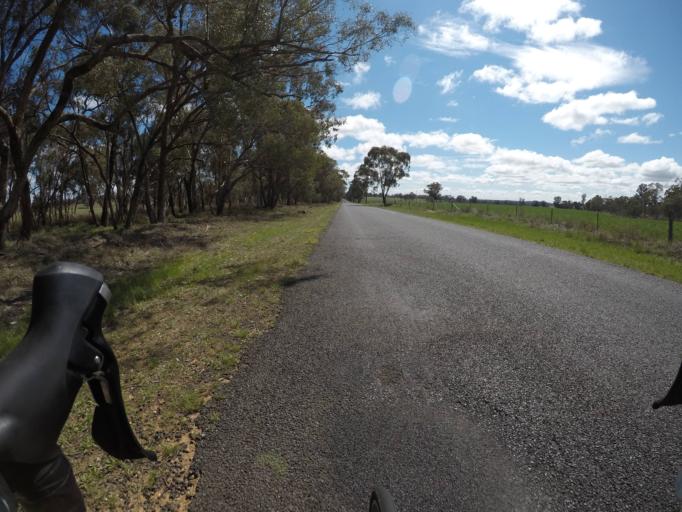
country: AU
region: New South Wales
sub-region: Dubbo Municipality
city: Dubbo
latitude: -32.5274
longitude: 148.5518
